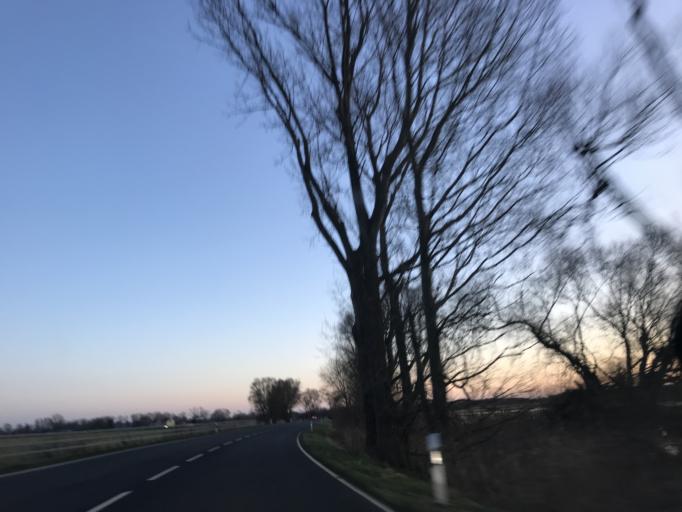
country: DE
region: Brandenburg
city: Premnitz
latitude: 52.5095
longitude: 12.4380
